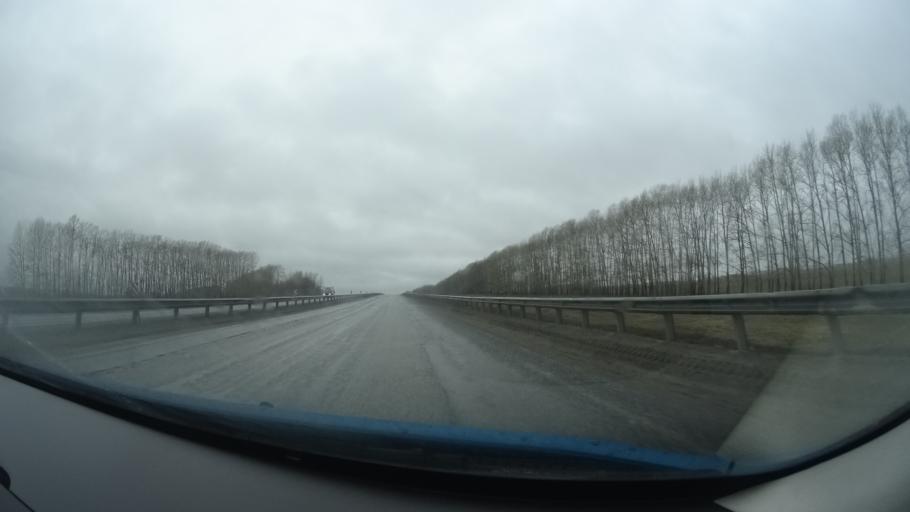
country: RU
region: Bashkortostan
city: Alekseyevka
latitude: 54.7161
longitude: 55.1970
